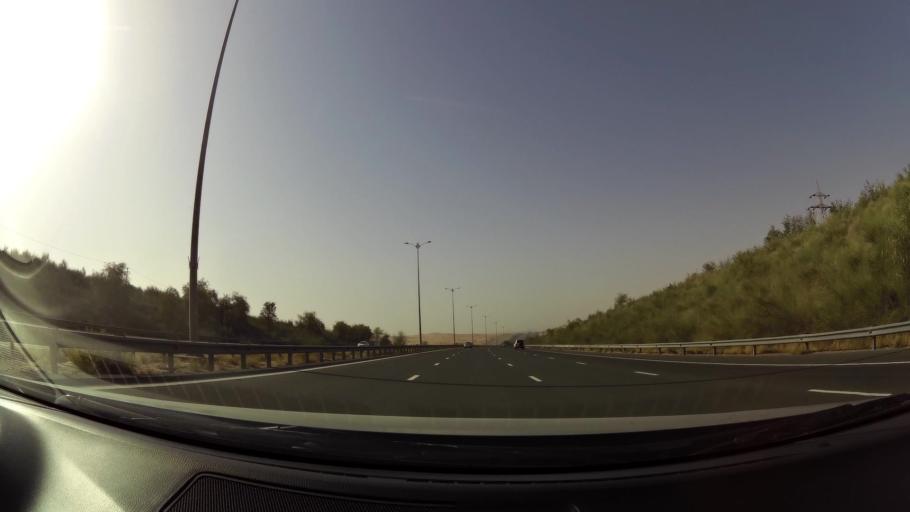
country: OM
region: Al Buraimi
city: Al Buraymi
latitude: 24.6309
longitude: 55.7206
